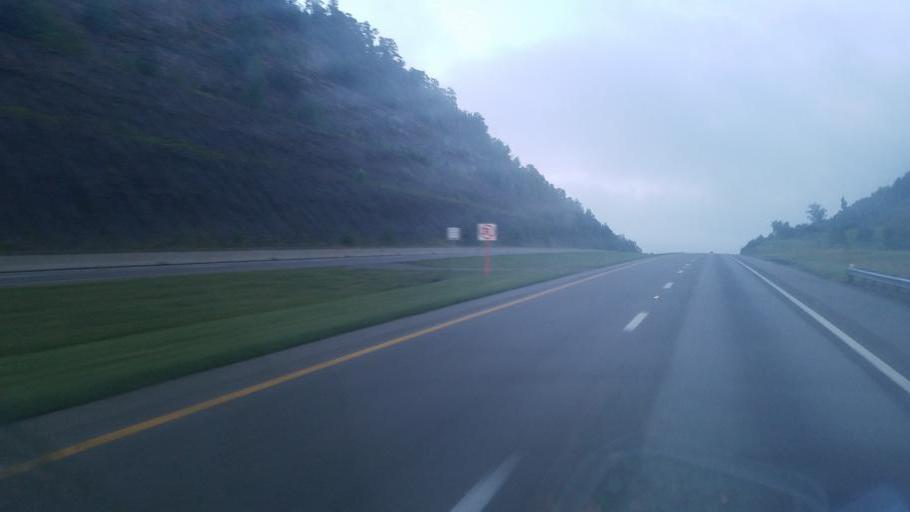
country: US
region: Ohio
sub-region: Ross County
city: Chillicothe
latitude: 39.2298
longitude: -82.8335
